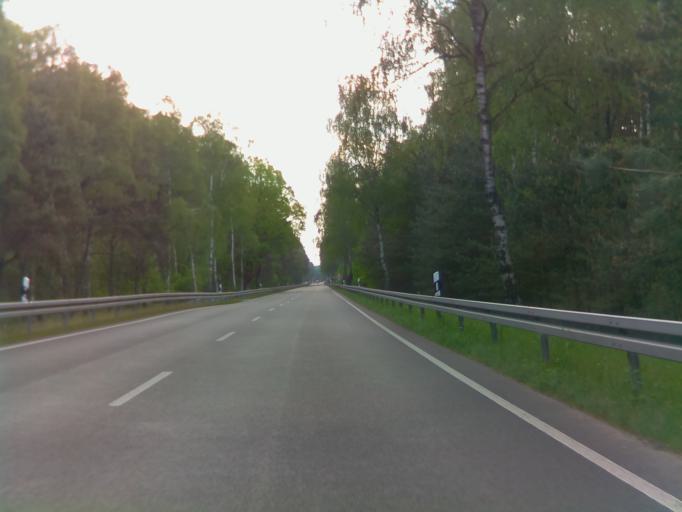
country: DE
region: Saxony-Anhalt
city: Schollene
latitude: 52.5728
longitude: 12.1967
